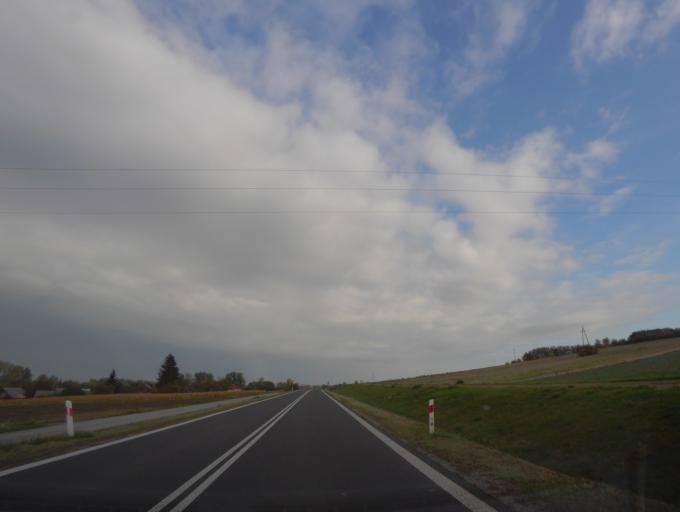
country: PL
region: Lublin Voivodeship
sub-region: Powiat lubelski
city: Wysokie
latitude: 50.8853
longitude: 22.6669
